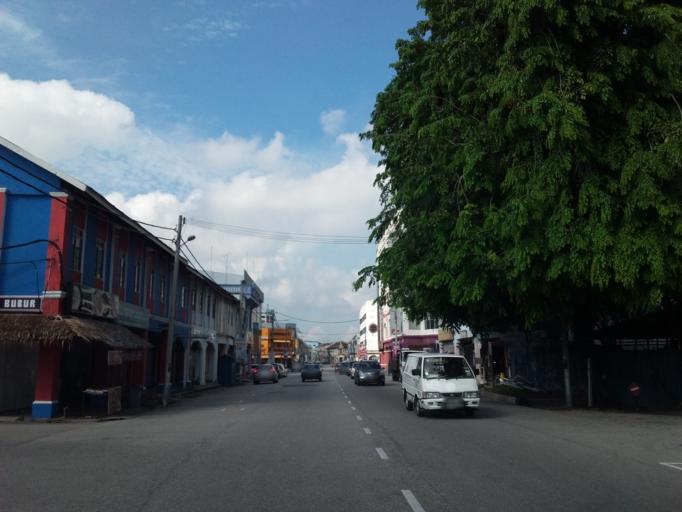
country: MY
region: Johor
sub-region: Daerah Batu Pahat
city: Batu Pahat
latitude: 1.8539
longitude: 102.9290
